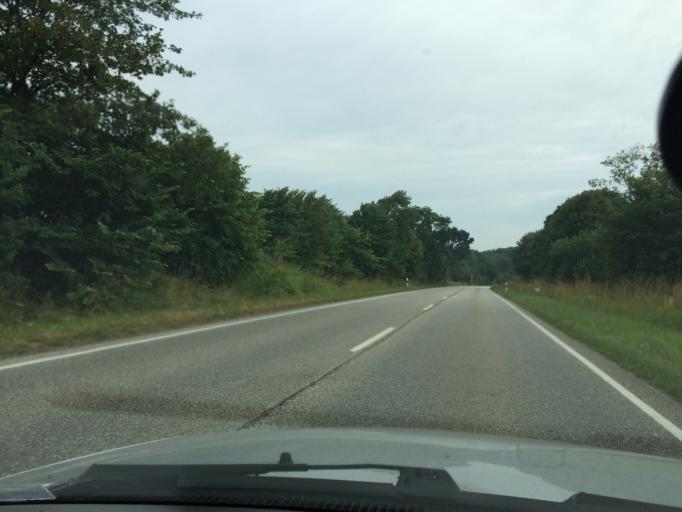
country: DE
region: Schleswig-Holstein
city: Oeversee
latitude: 54.7105
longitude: 9.4396
